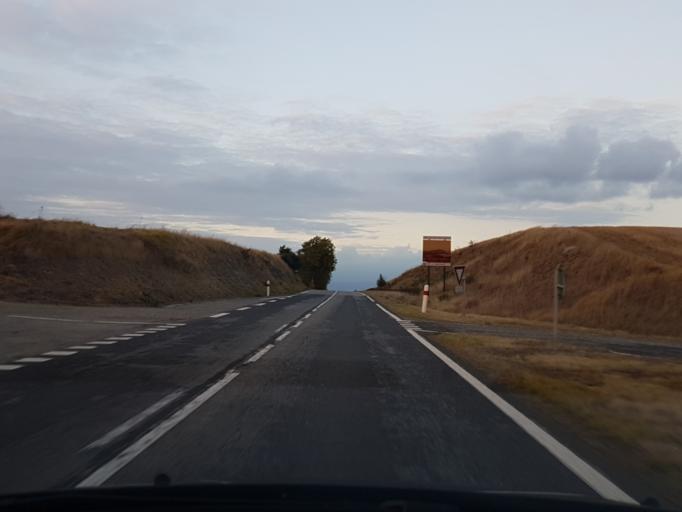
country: FR
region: Languedoc-Roussillon
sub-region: Departement de l'Aude
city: Saint-Martin-Lalande
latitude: 43.1643
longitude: 1.9937
